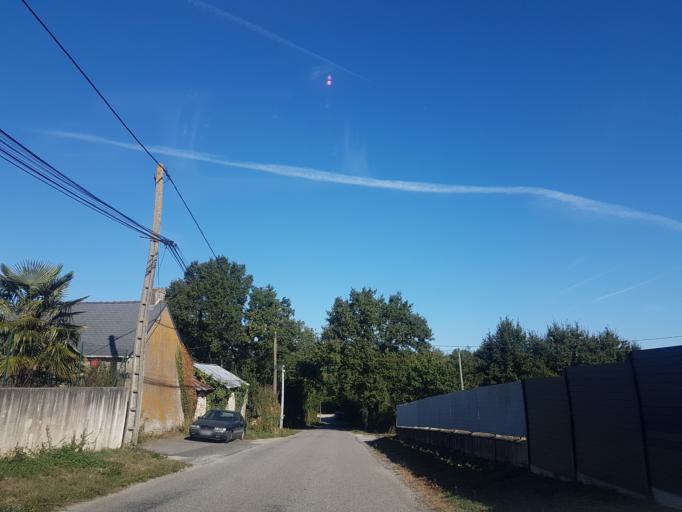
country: FR
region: Pays de la Loire
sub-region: Departement de la Loire-Atlantique
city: Petit-Mars
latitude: 47.3911
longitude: -1.4448
